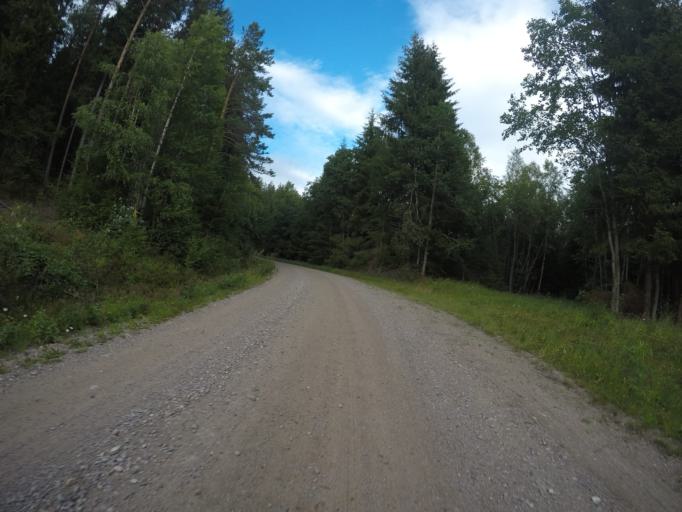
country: SE
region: Vaermland
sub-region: Filipstads Kommun
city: Lesjofors
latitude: 60.0104
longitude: 14.4228
